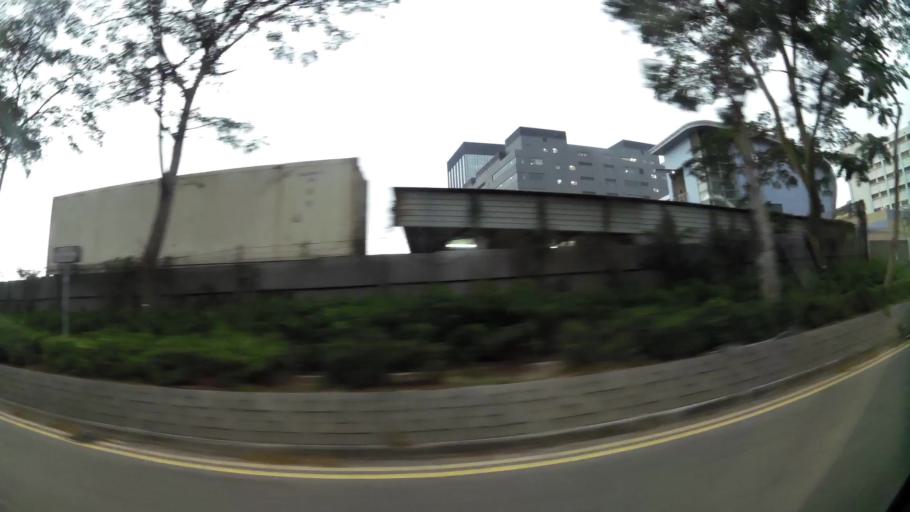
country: HK
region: Tsuen Wan
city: Tsuen Wan
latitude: 22.3360
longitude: 114.1082
